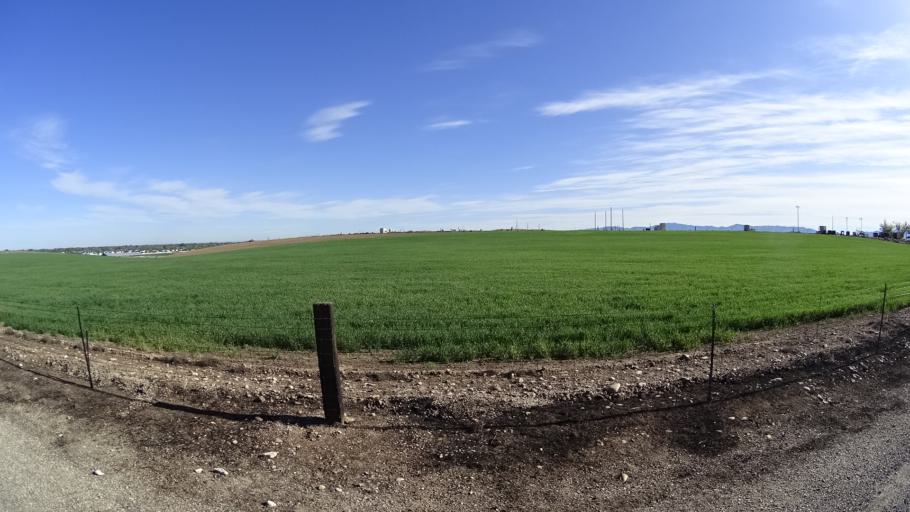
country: US
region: Idaho
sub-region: Ada County
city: Garden City
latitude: 43.5248
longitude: -116.2845
